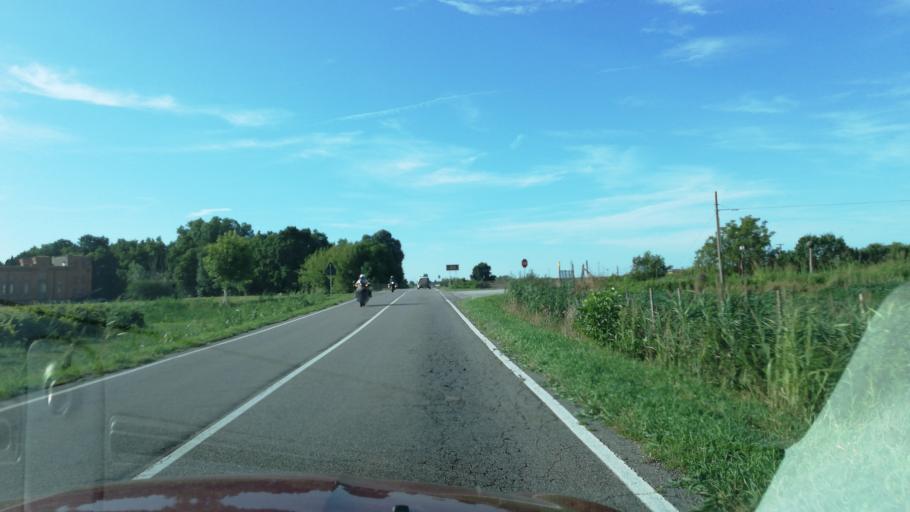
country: IT
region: Veneto
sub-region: Provincia di Venezia
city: La Salute di Livenza
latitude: 45.6021
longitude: 12.8045
